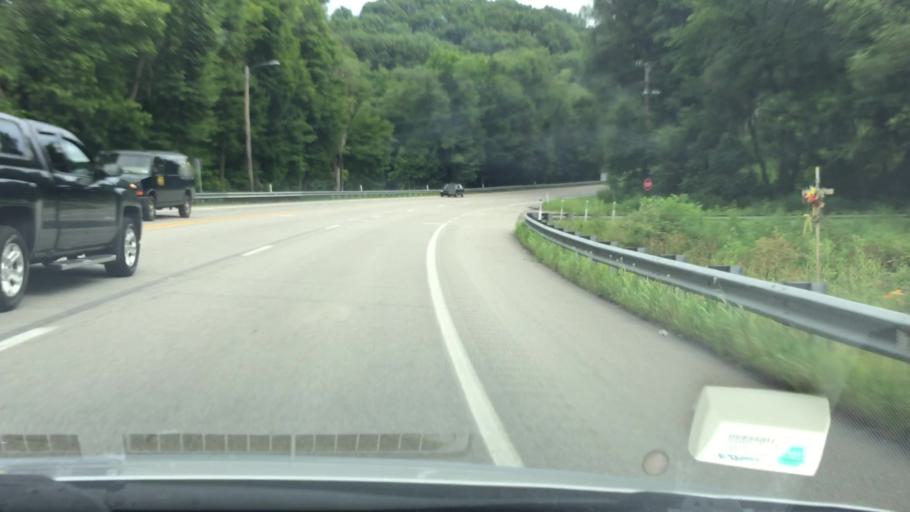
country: US
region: Pennsylvania
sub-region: Westmoreland County
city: New Kensington
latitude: 40.5774
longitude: -79.7504
